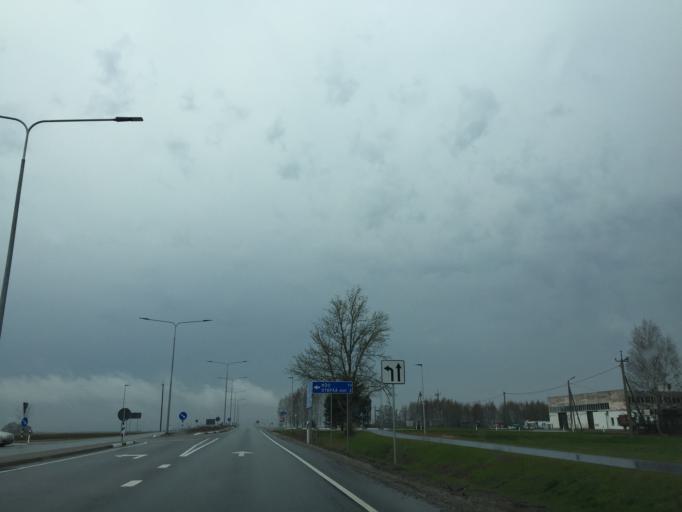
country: EE
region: Tartu
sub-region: UElenurme vald
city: Ulenurme
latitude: 58.2371
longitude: 26.6913
